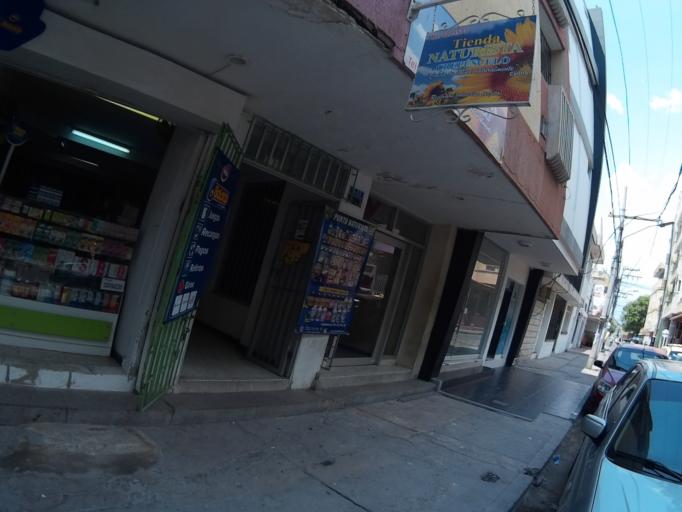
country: CO
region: Magdalena
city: Santa Marta
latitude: 11.2437
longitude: -74.2105
